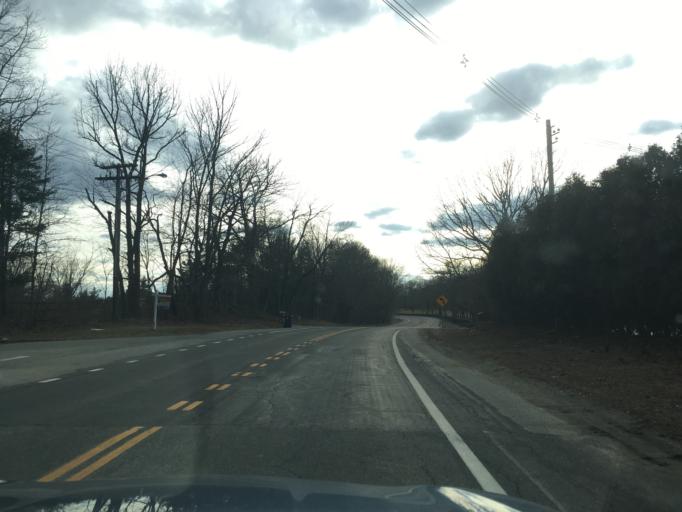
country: US
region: Rhode Island
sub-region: Kent County
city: East Greenwich
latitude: 41.6583
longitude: -71.4280
